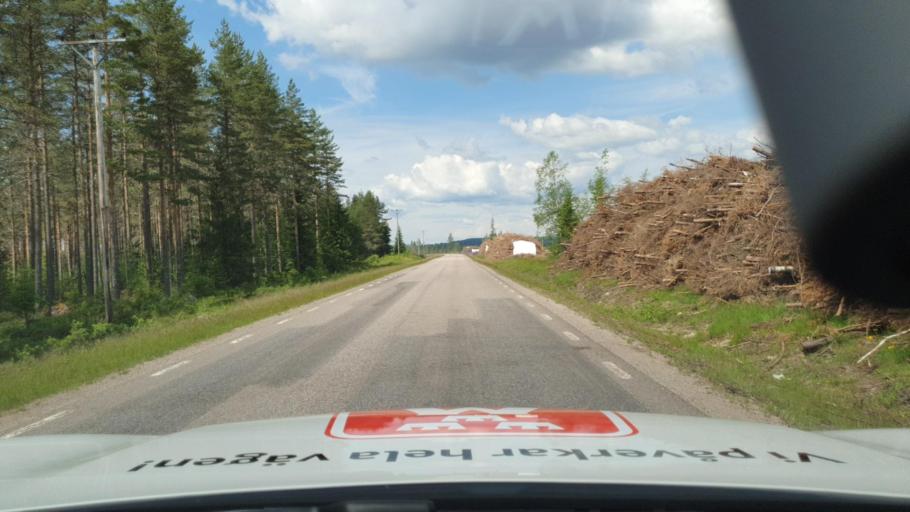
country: SE
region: Vaermland
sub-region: Torsby Kommun
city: Torsby
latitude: 60.5020
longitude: 12.8550
